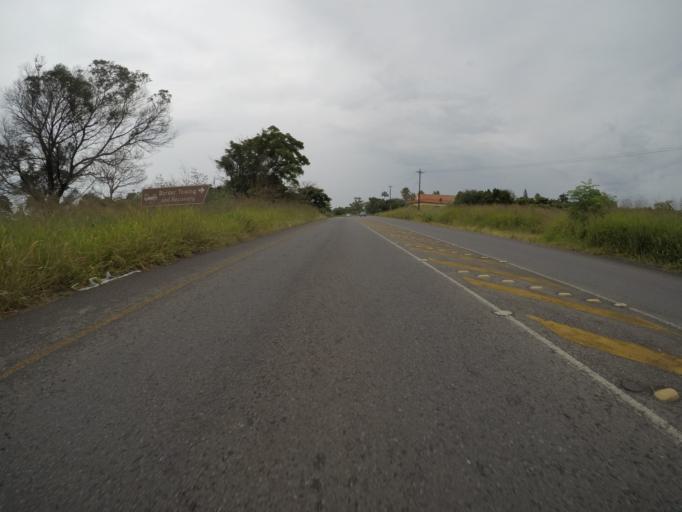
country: ZA
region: Eastern Cape
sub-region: Buffalo City Metropolitan Municipality
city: East London
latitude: -32.9654
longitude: 27.8402
